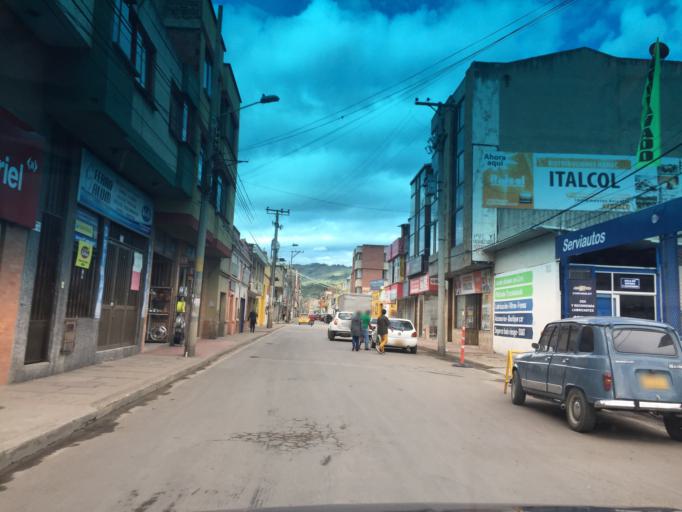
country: CO
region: Boyaca
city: Duitama
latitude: 5.8232
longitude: -73.0354
